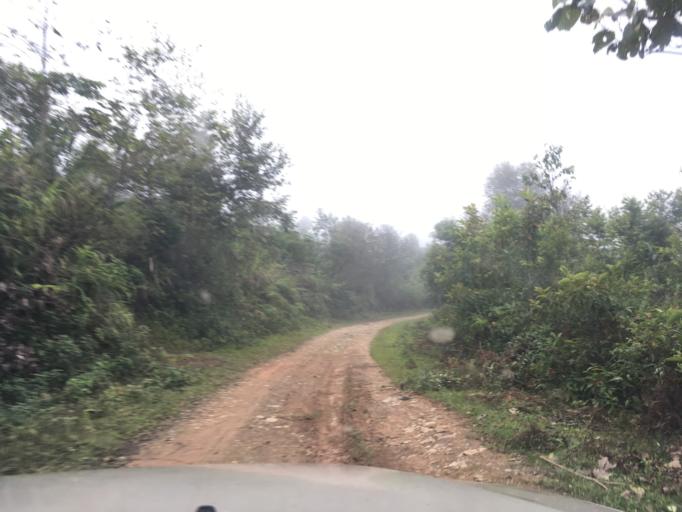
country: LA
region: Phongsali
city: Phongsali
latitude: 21.4279
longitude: 102.2637
